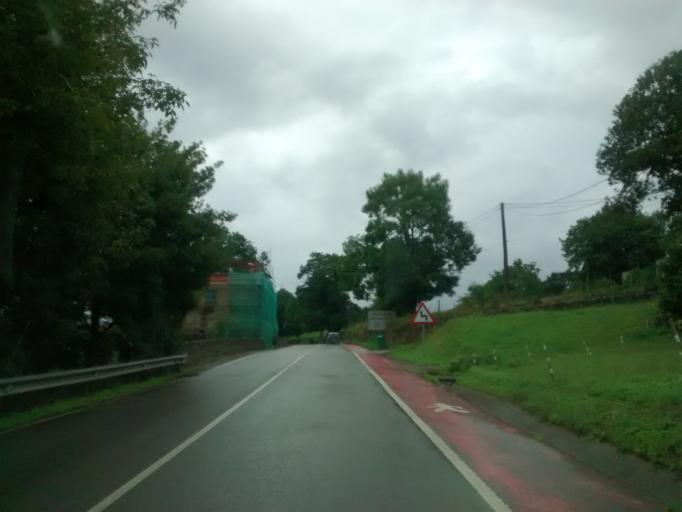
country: ES
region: Cantabria
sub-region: Provincia de Cantabria
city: Entrambasaguas
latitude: 43.3568
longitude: -3.7031
